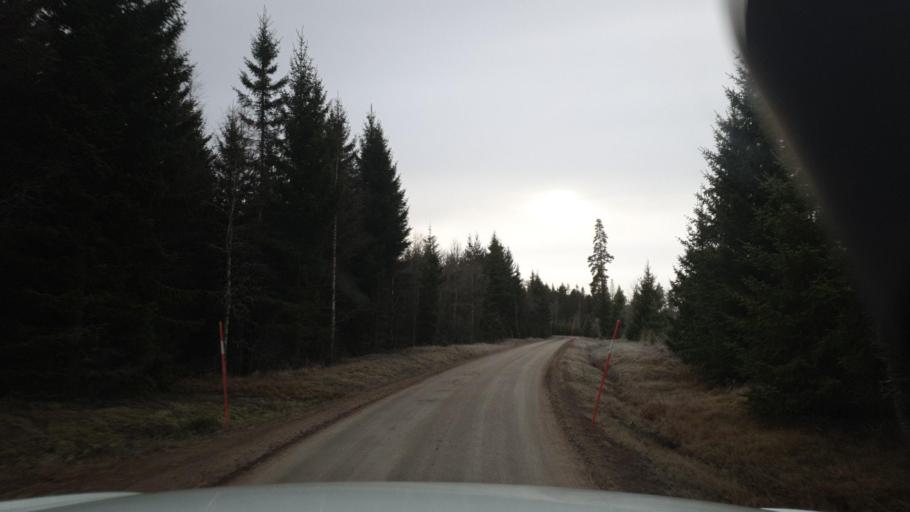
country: SE
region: Vaermland
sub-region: Sunne Kommun
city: Sunne
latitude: 59.8257
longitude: 12.8437
